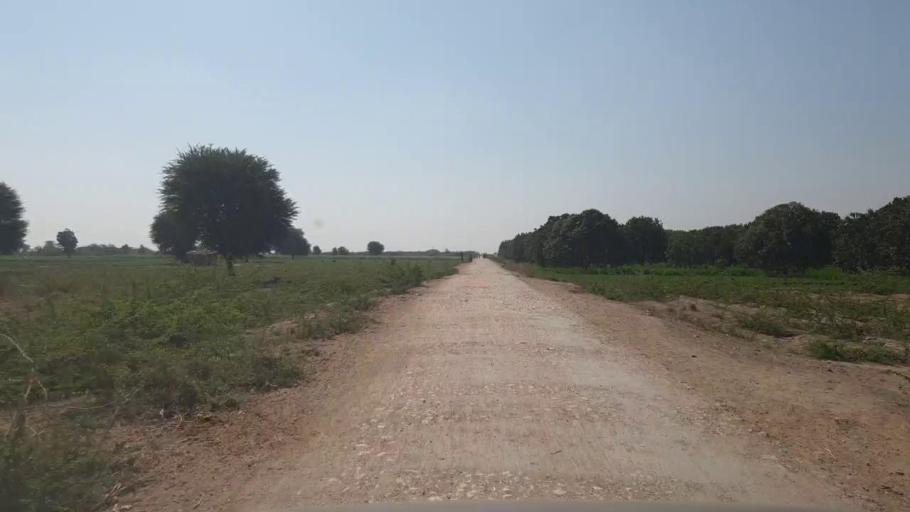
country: PK
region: Sindh
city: Digri
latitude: 25.2383
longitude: 69.2251
